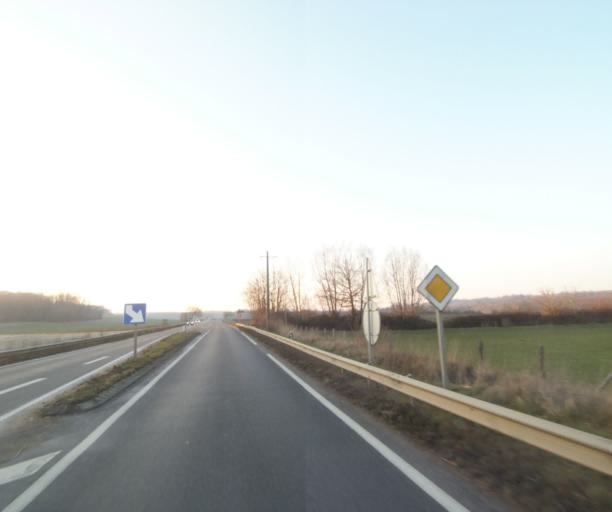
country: FR
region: Lorraine
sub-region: Departement de la Meuse
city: Ancerville
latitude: 48.6058
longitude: 5.0249
